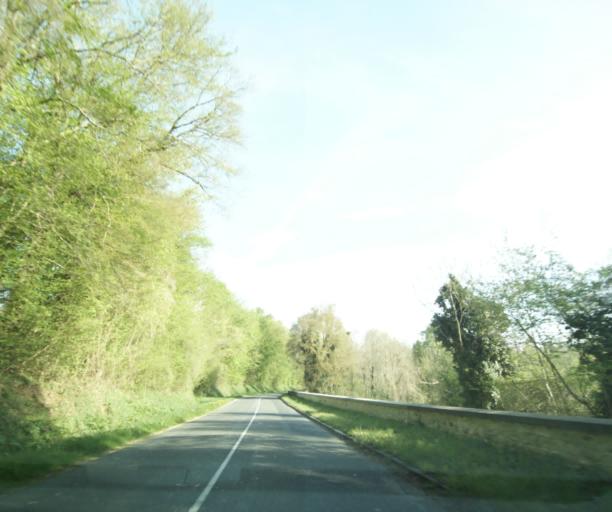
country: FR
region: Ile-de-France
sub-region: Departement de Seine-et-Marne
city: Vernou-la-Celle-sur-Seine
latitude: 48.4526
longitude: 2.8595
